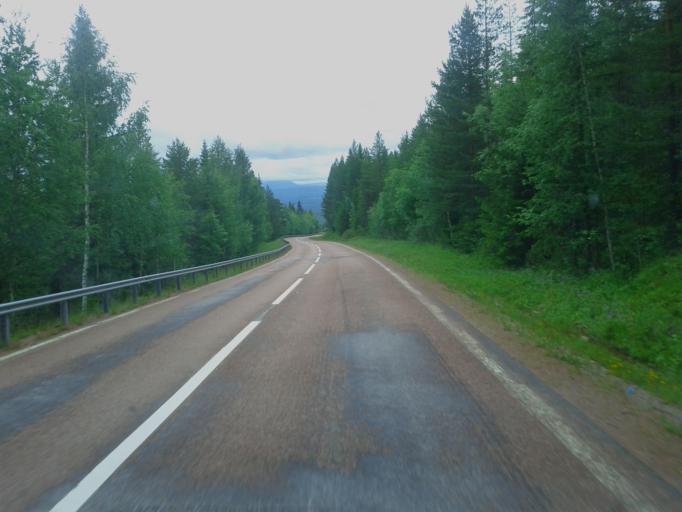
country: NO
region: Hedmark
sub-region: Trysil
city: Innbygda
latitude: 61.8465
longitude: 12.6019
